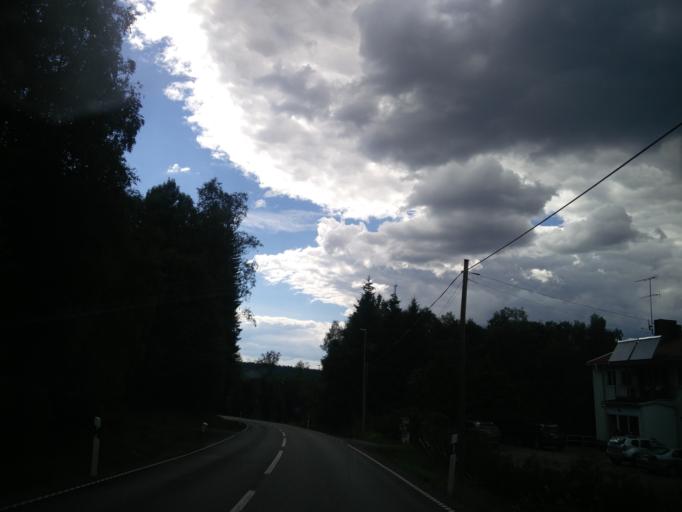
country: SE
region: OErebro
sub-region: Hallefors Kommun
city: Haellefors
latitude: 59.8047
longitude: 14.5910
